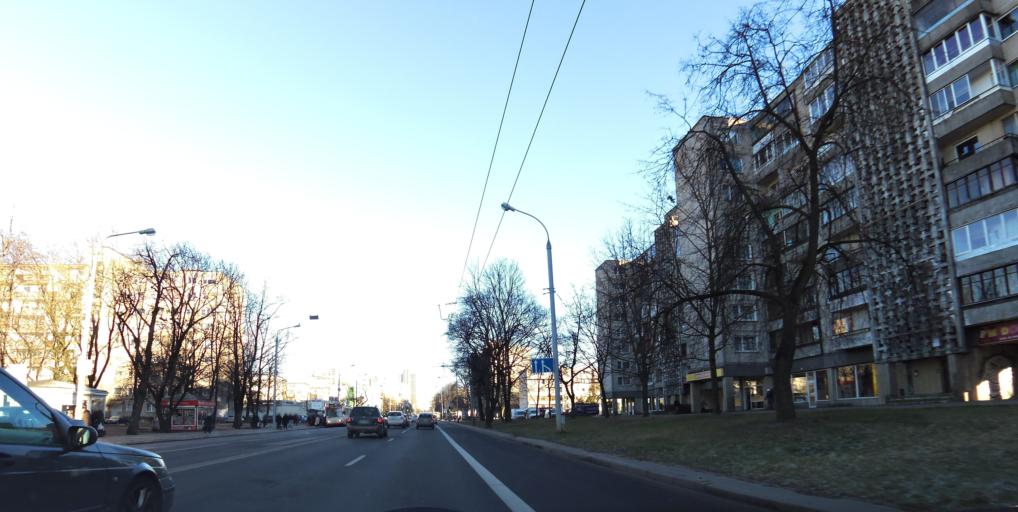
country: LT
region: Vilnius County
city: Vilkpede
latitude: 54.6729
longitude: 25.2463
